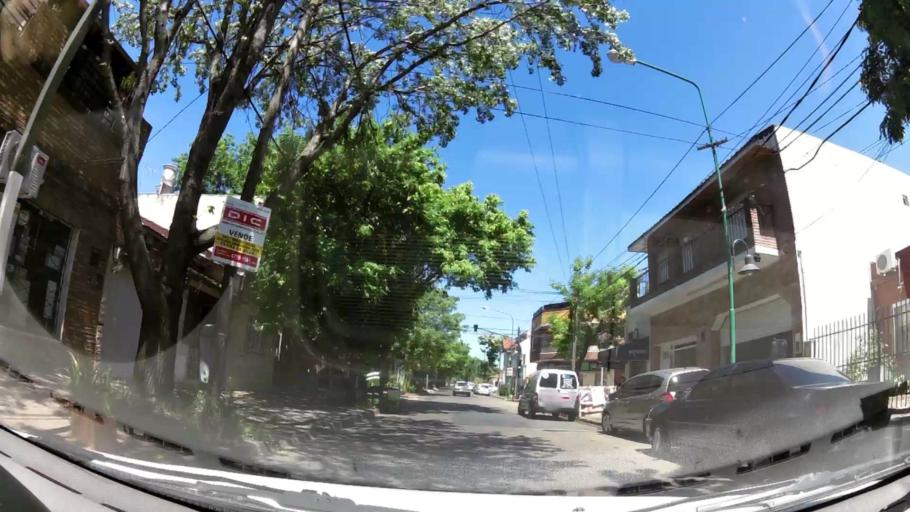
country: AR
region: Buenos Aires
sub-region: Partido de Vicente Lopez
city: Olivos
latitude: -34.5133
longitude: -58.5031
